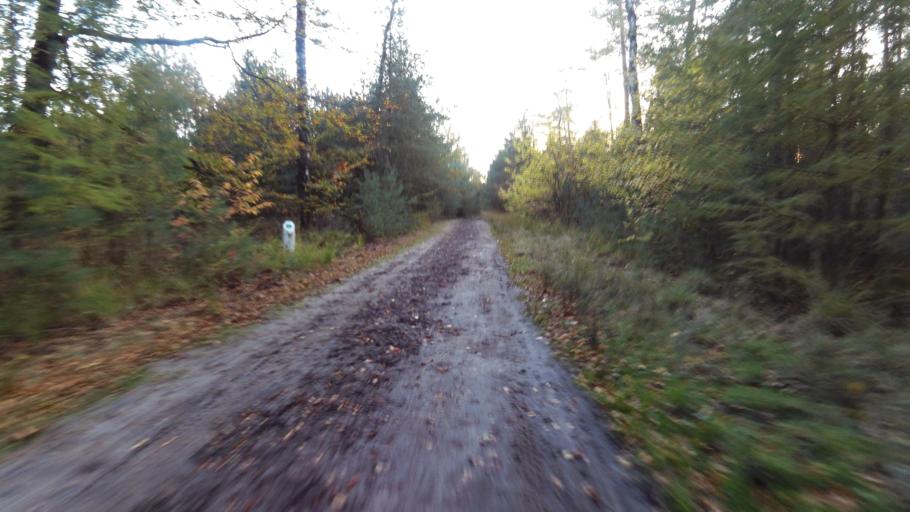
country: NL
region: Gelderland
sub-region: Gemeente Epe
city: Epe
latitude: 52.3683
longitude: 5.9417
